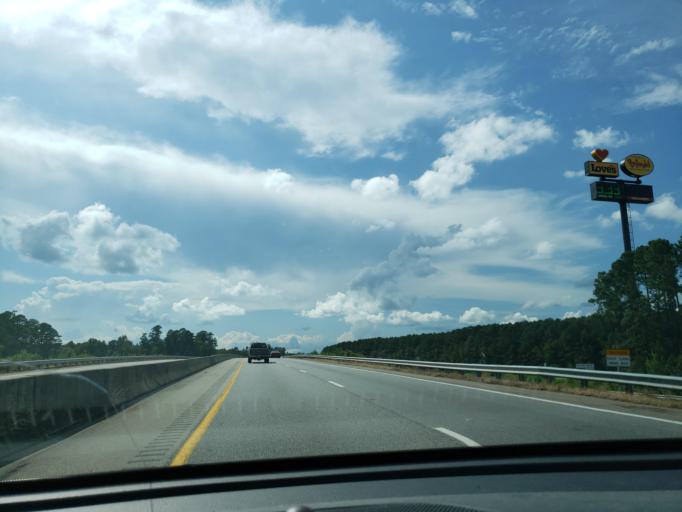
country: US
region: Virginia
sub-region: City of Franklin
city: Franklin
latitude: 36.6606
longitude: -76.9398
